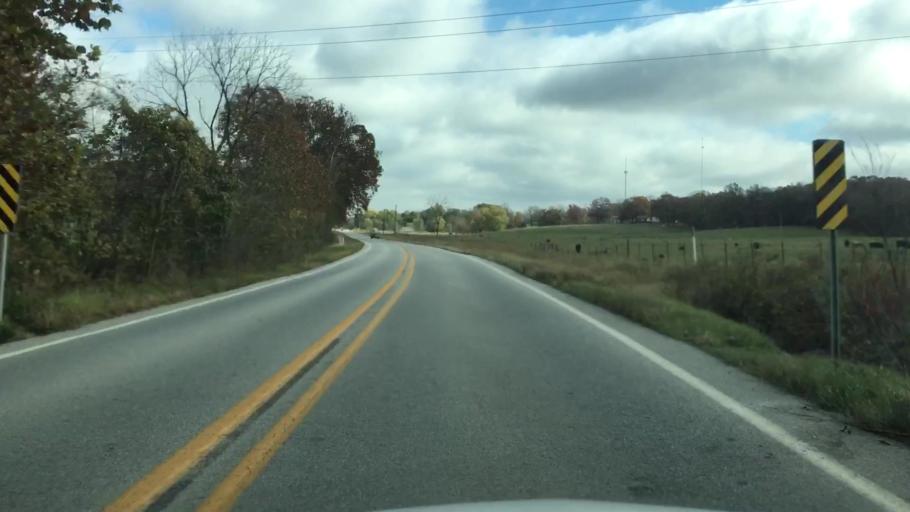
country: US
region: Arkansas
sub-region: Benton County
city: Gentry
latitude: 36.2576
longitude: -94.4028
